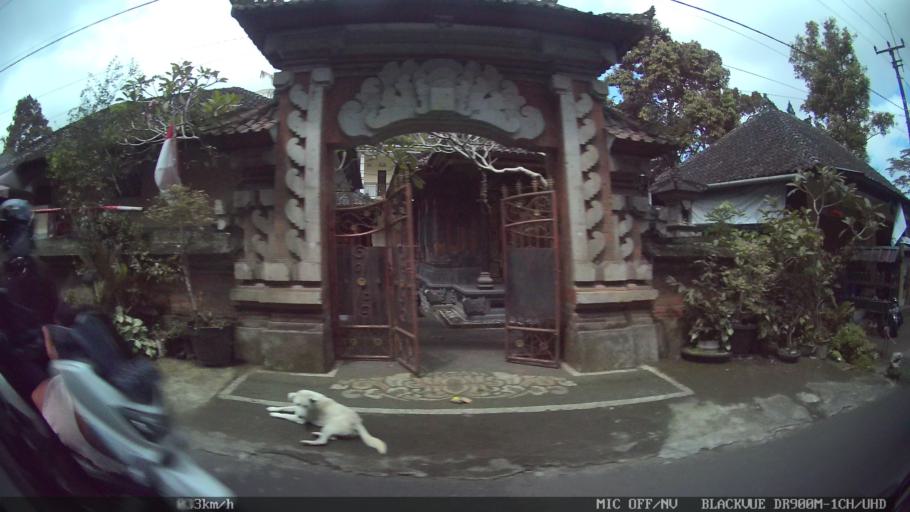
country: ID
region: Bali
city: Bangli
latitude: -8.4528
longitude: 115.3444
